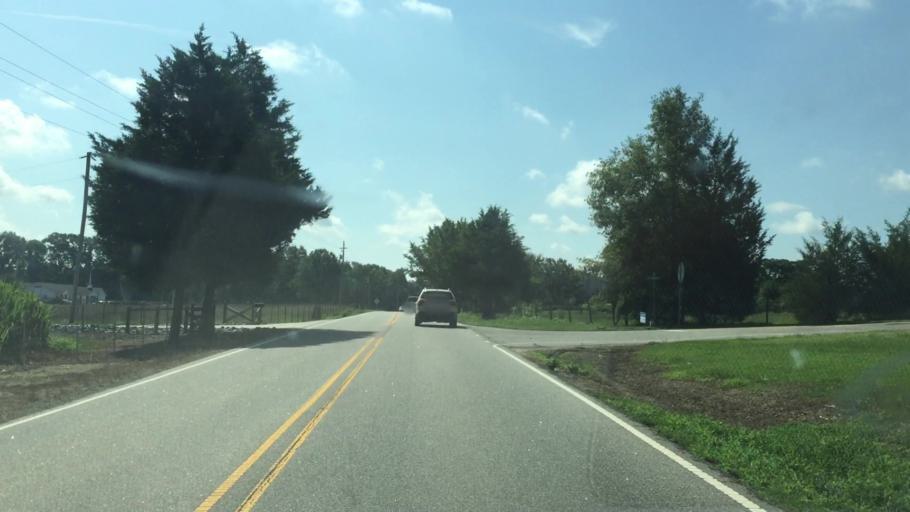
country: US
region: North Carolina
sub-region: Anson County
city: Burnsville
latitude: 35.0632
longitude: -80.2796
